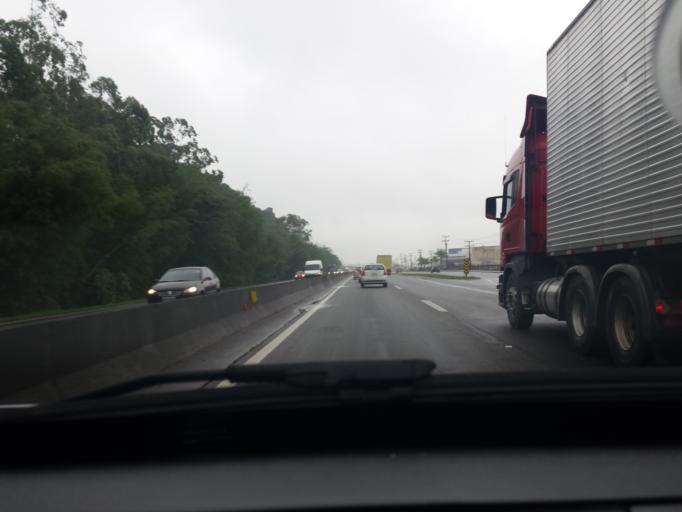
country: BR
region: Santa Catarina
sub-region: Itajai
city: Itajai
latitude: -26.9288
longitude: -48.7052
